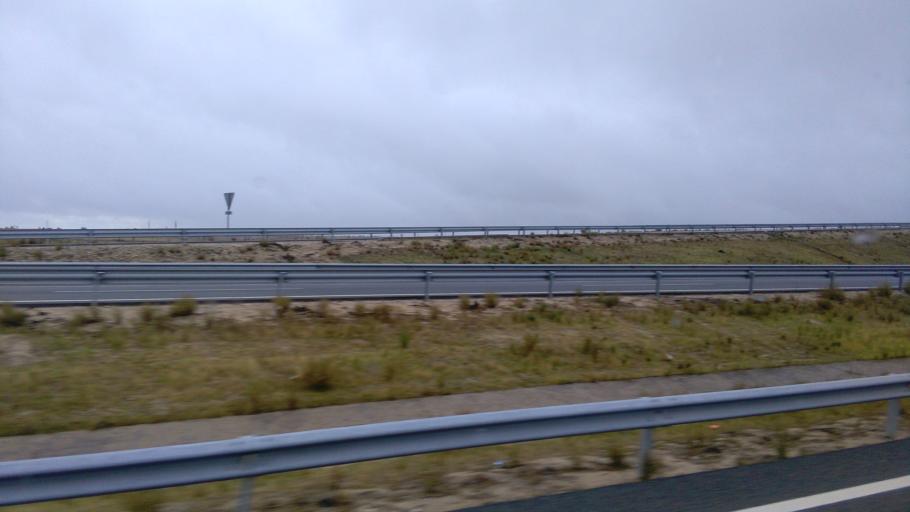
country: ES
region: Castille-La Mancha
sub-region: Province of Toledo
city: Las Ventas de Retamosa
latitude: 40.1781
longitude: -4.1461
